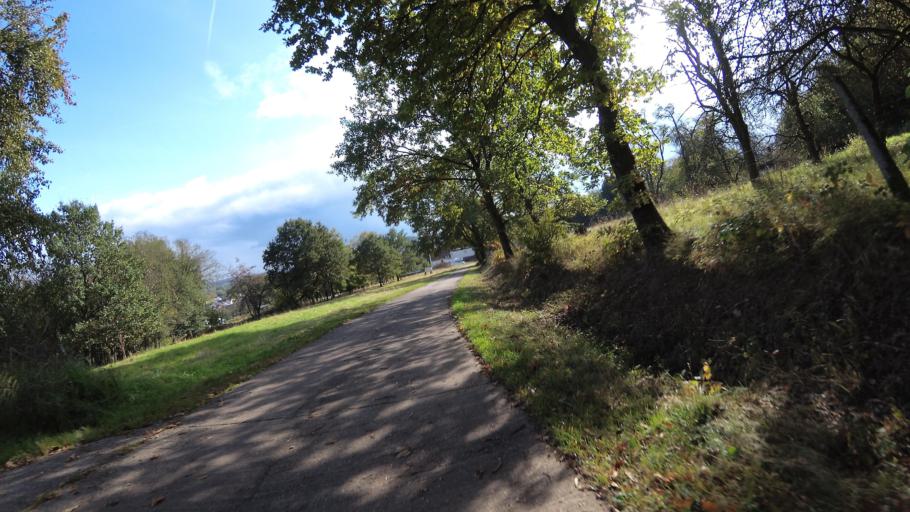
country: DE
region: Rheinland-Pfalz
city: Altenkirchen
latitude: 49.4465
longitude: 7.3184
